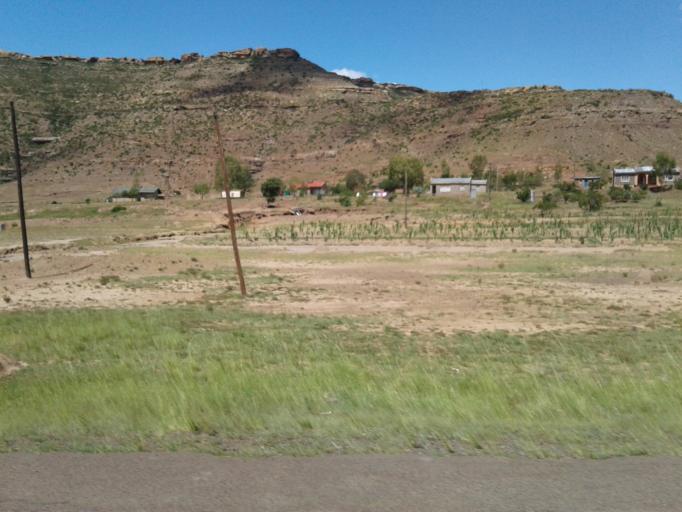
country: LS
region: Quthing
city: Quthing
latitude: -30.3327
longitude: 27.5335
